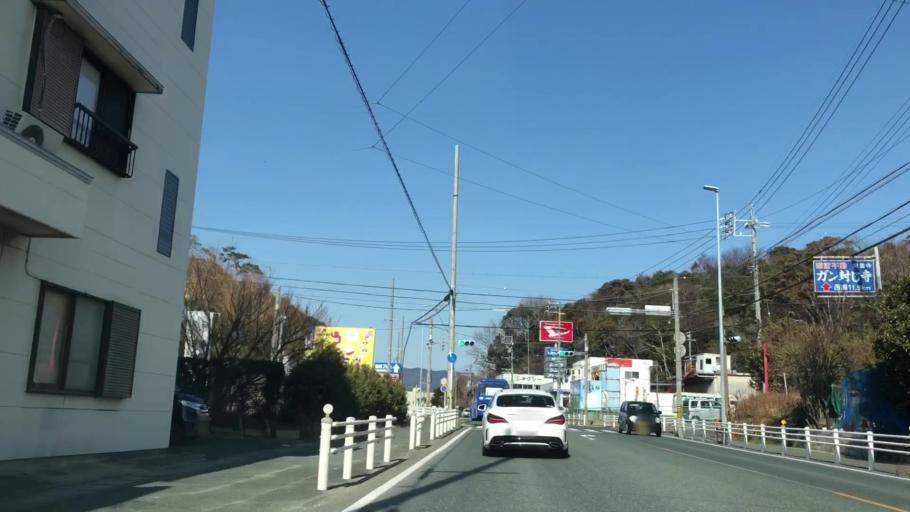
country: JP
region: Aichi
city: Gamagori
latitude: 34.8077
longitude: 137.2583
